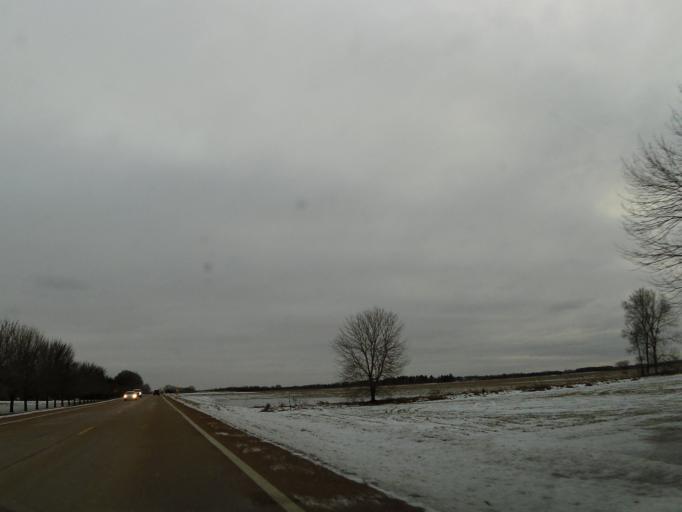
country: US
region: Minnesota
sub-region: Scott County
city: Jordan
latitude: 44.7140
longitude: -93.6490
